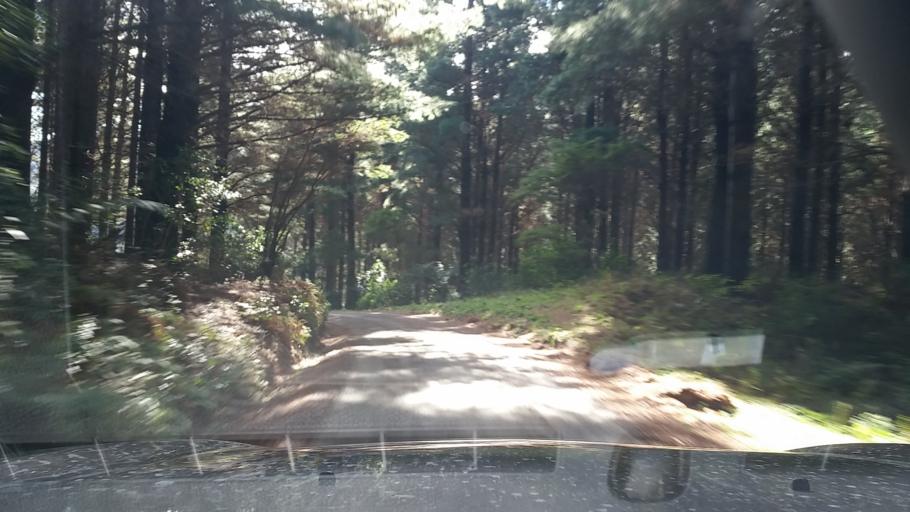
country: NZ
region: Marlborough
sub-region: Marlborough District
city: Picton
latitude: -41.1576
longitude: 173.9710
